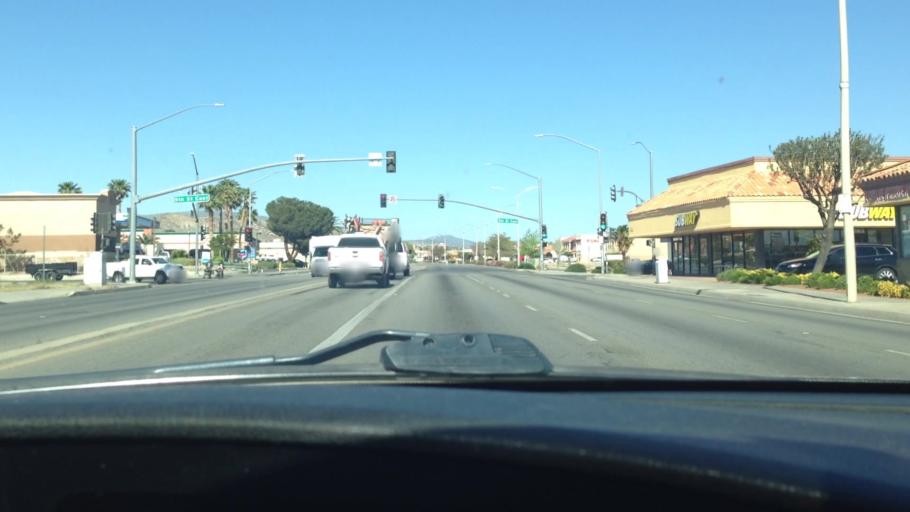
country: US
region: California
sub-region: Los Angeles County
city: Palmdale
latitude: 34.5796
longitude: -118.1199
